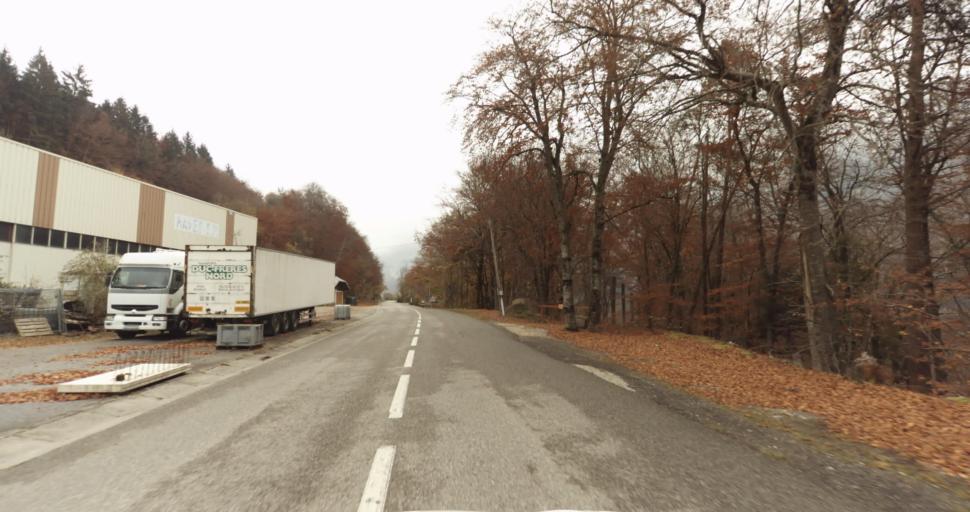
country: FR
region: Rhone-Alpes
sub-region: Departement de la Haute-Savoie
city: Gruffy
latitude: 45.7576
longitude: 6.0679
